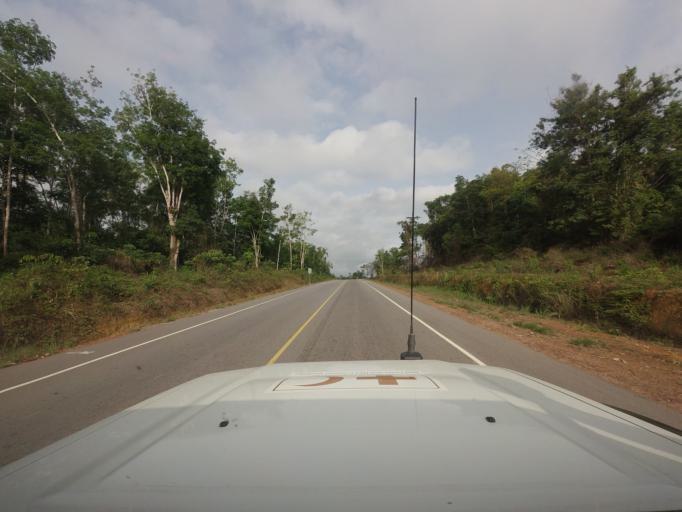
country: LR
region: Bong
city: Gbarnga
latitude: 7.0039
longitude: -9.2977
